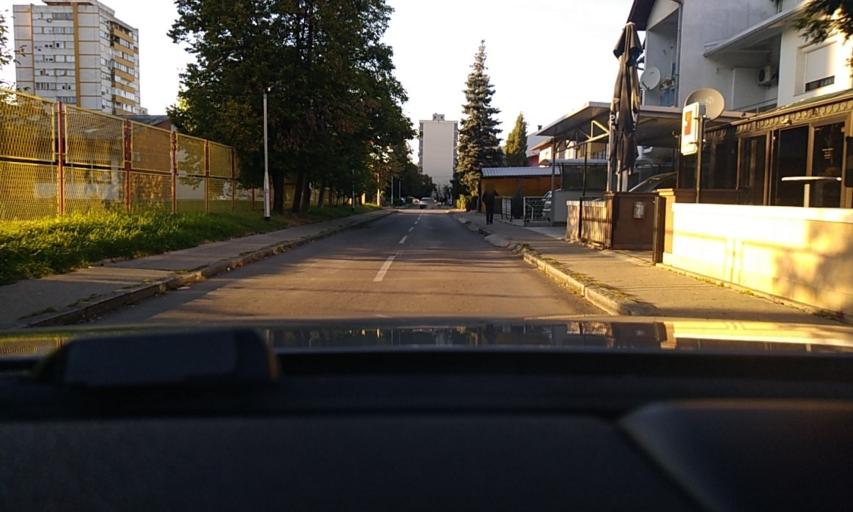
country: BA
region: Republika Srpska
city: Starcevica
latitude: 44.7704
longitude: 17.2084
